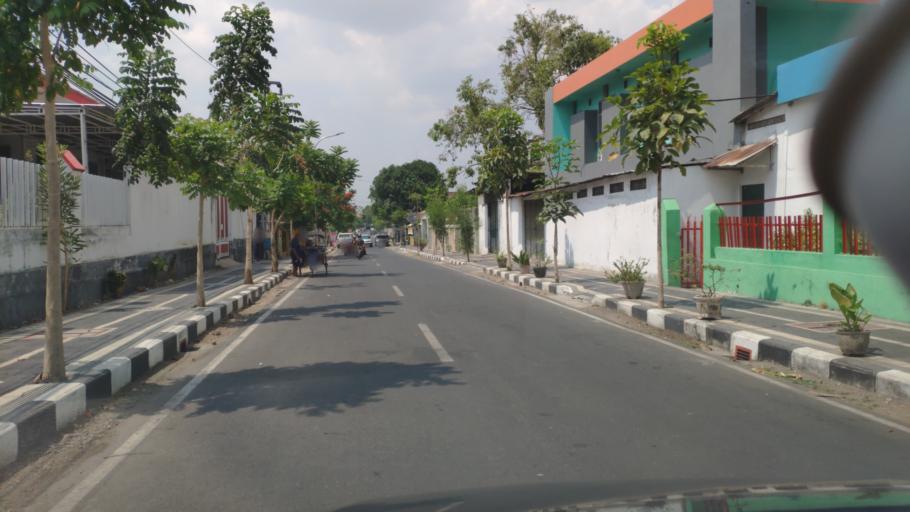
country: ID
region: Central Java
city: Blora
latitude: -6.9695
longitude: 111.4150
